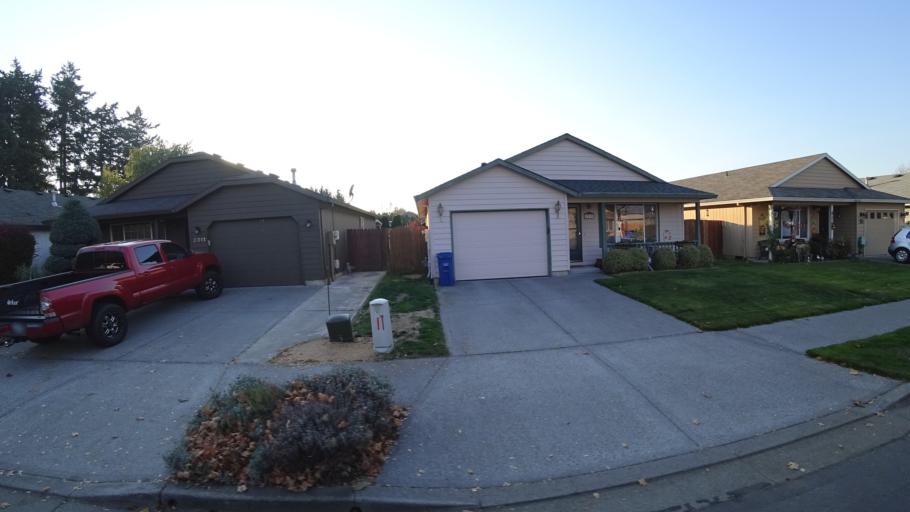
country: US
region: Oregon
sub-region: Multnomah County
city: Gresham
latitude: 45.5131
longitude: -122.4353
